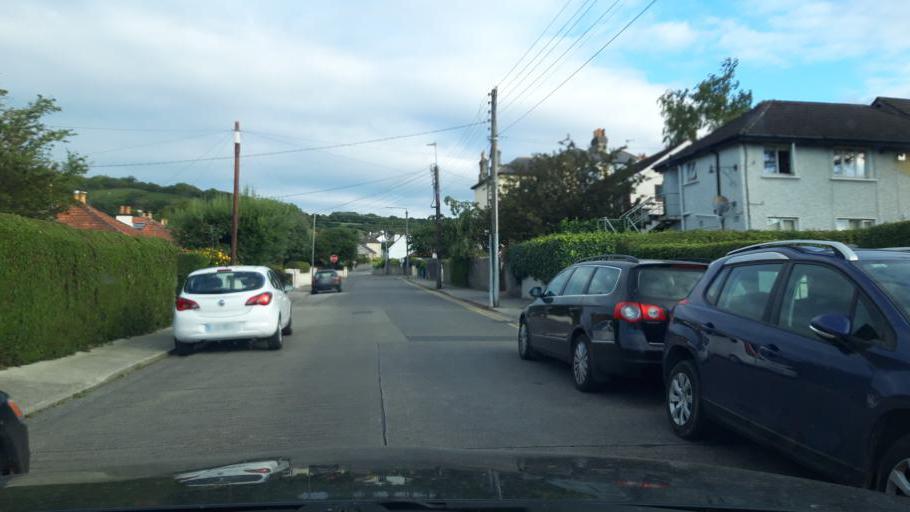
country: IE
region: Leinster
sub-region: Wicklow
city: Bray
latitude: 53.1962
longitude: -6.0991
